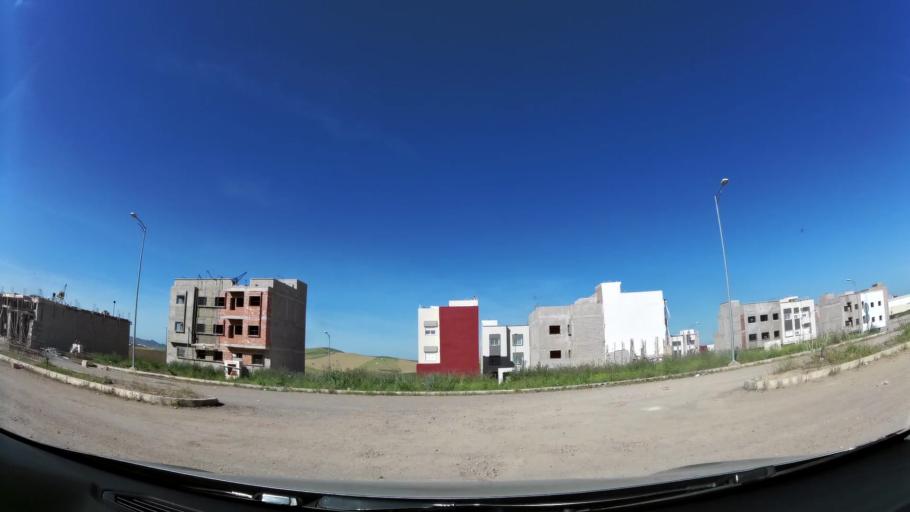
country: MA
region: Fes-Boulemane
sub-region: Fes
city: Fes
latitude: 34.0137
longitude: -4.9595
